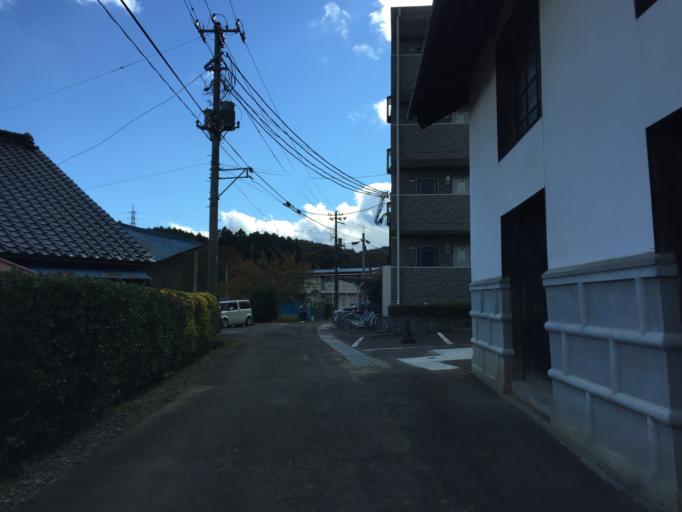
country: JP
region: Fukushima
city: Fukushima-shi
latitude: 37.6742
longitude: 140.4535
